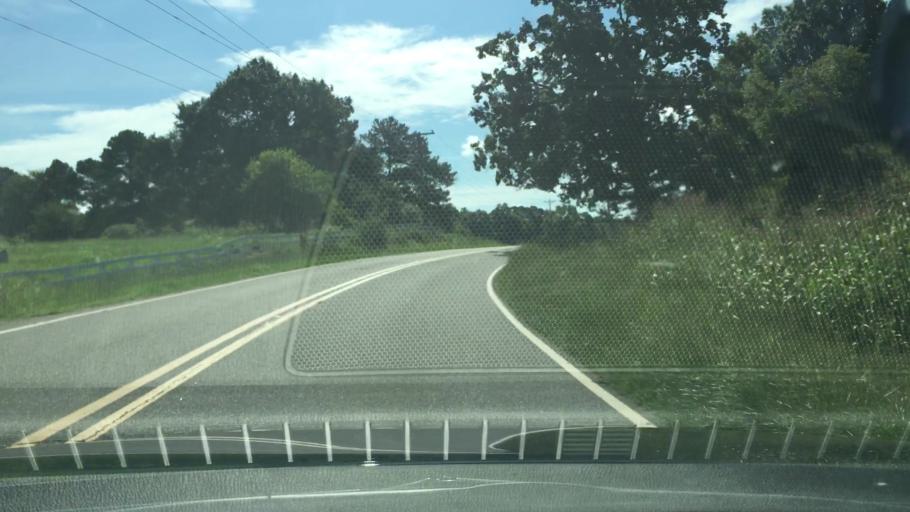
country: US
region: Georgia
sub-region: Putnam County
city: Jefferson
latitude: 33.4412
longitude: -83.3455
